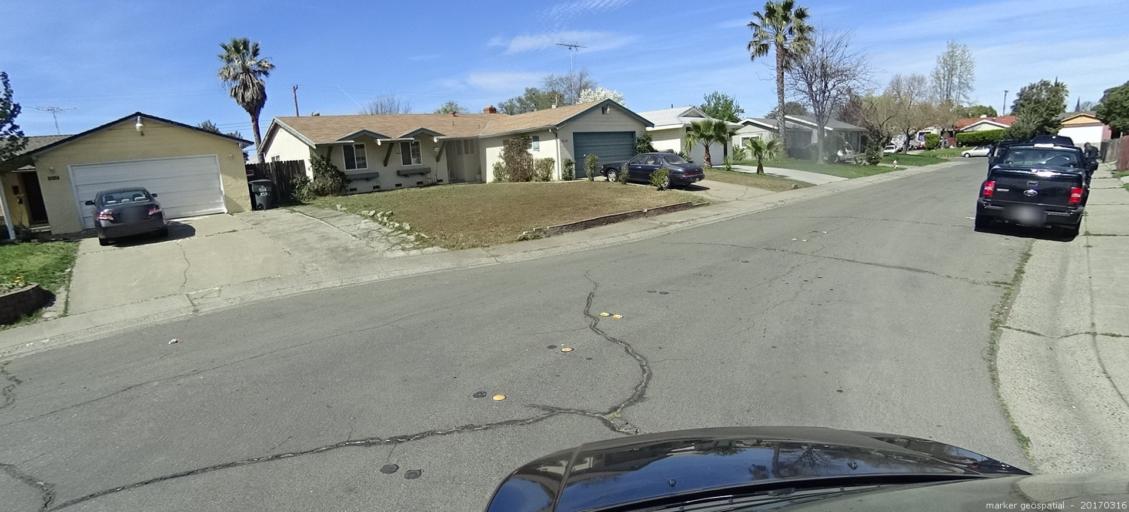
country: US
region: California
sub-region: Sacramento County
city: Parkway
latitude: 38.4780
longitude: -121.4858
